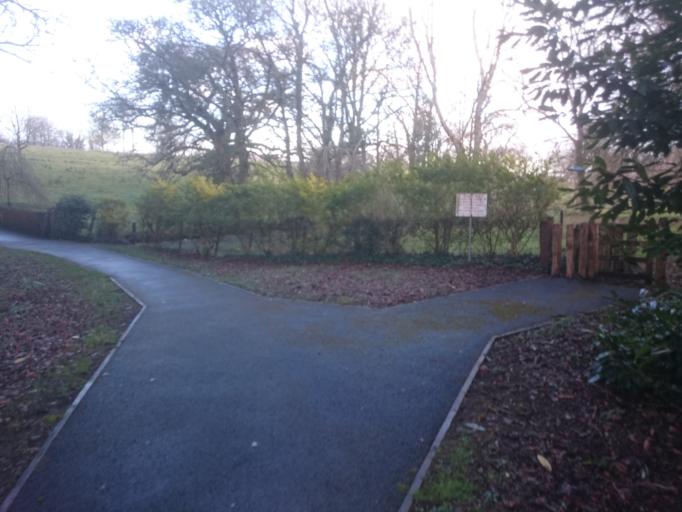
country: IE
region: Connaught
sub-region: Roscommon
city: Castlerea
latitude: 53.7682
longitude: -8.4860
